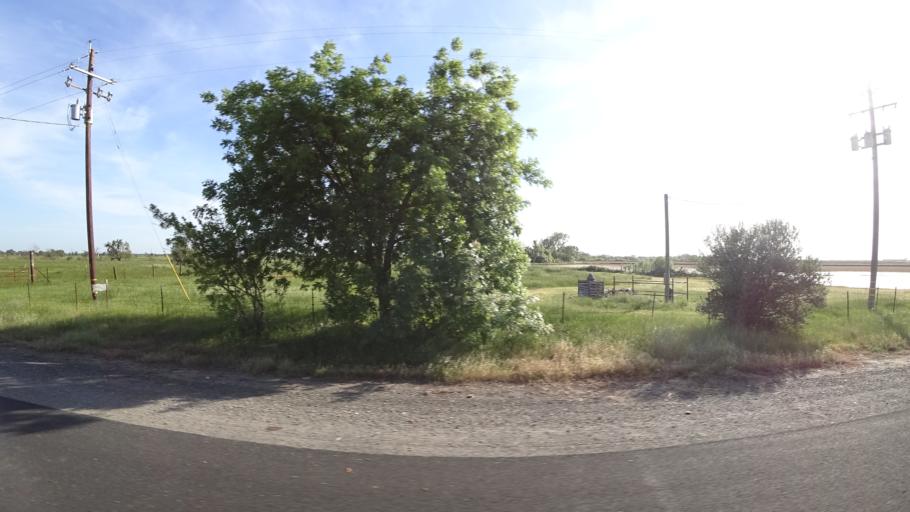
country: US
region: California
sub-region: Yuba County
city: Wheatland
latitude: 39.0371
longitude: -121.4664
